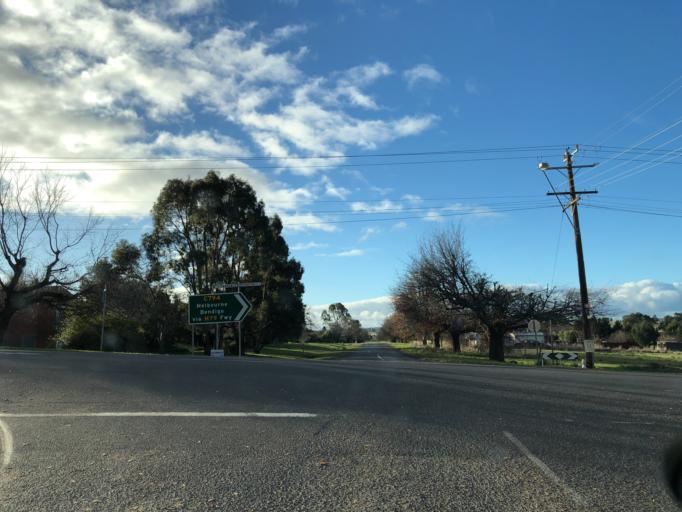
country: AU
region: Victoria
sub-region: Mount Alexander
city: Castlemaine
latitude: -37.1878
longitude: 144.3754
